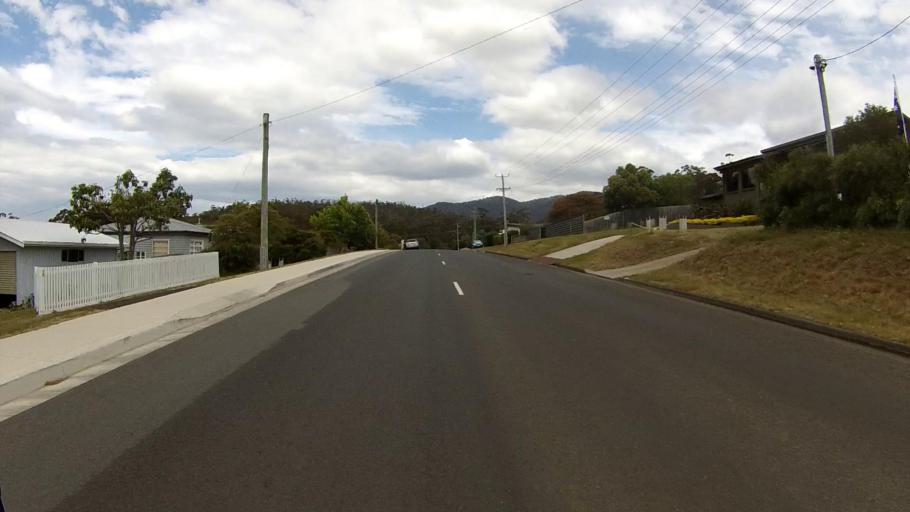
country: AU
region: Tasmania
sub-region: Sorell
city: Sorell
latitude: -42.5646
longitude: 147.8733
